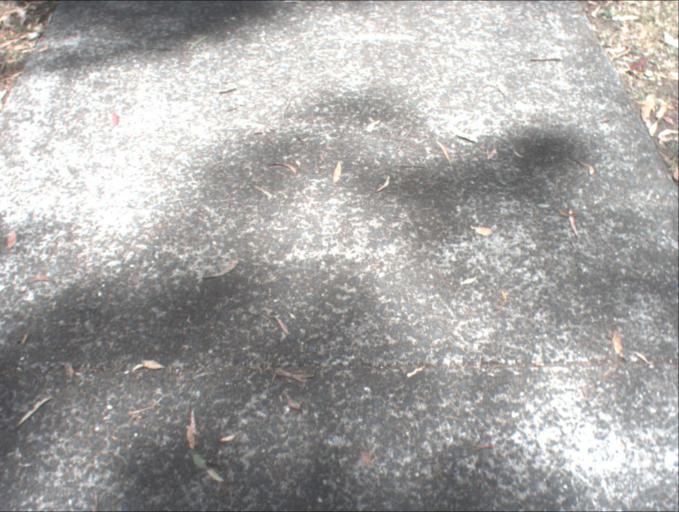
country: AU
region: Queensland
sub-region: Logan
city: Slacks Creek
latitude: -27.6537
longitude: 153.1683
